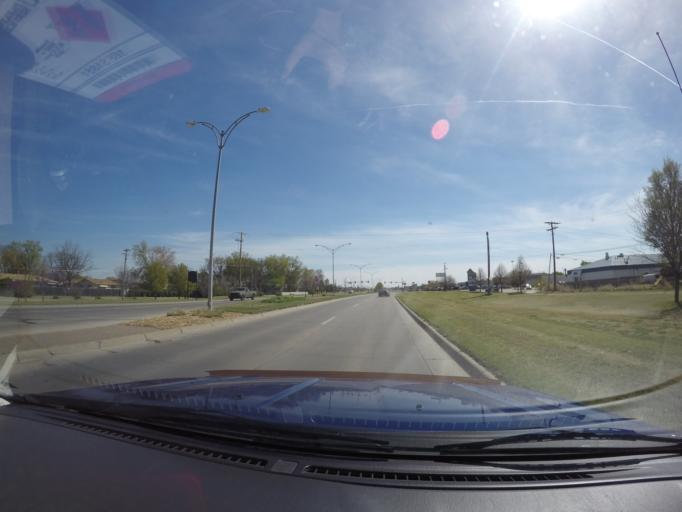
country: US
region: Kansas
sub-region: Saline County
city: Salina
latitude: 38.8064
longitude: -97.6128
